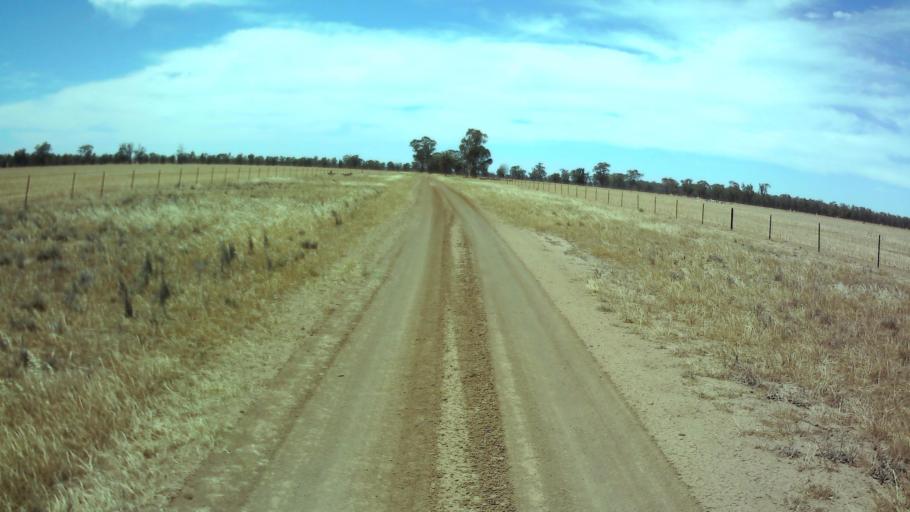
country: AU
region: New South Wales
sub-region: Weddin
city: Grenfell
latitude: -33.8967
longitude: 147.8022
